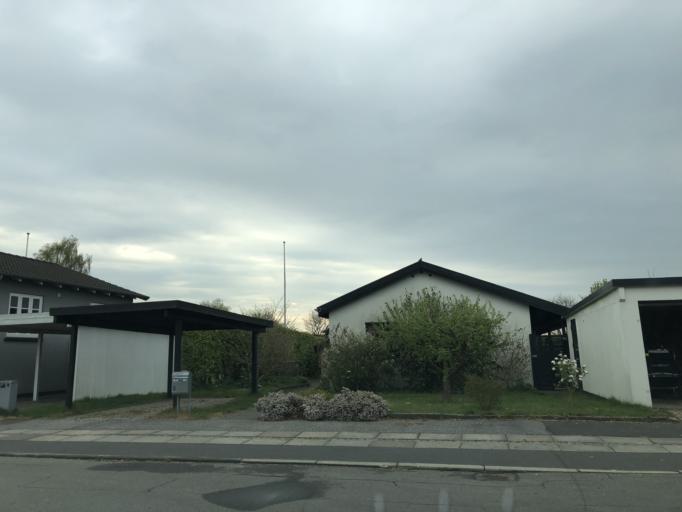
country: DK
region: Central Jutland
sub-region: Holstebro Kommune
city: Holstebro
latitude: 56.3606
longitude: 8.6323
